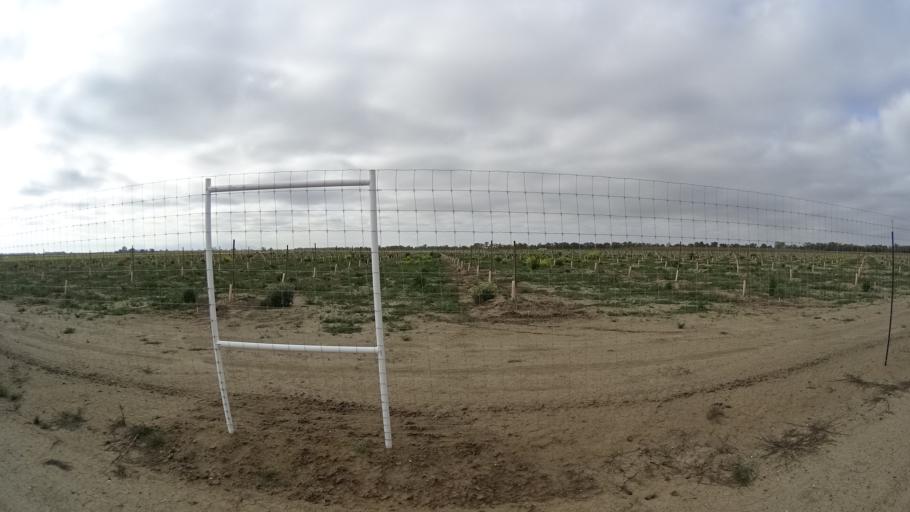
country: US
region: California
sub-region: Colusa County
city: Colusa
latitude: 39.4185
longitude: -121.9790
